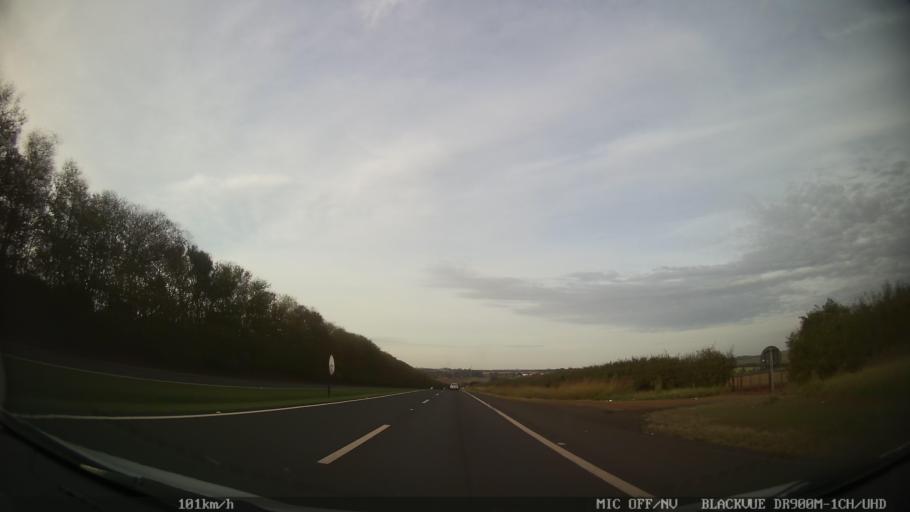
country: BR
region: Sao Paulo
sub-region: Iracemapolis
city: Iracemapolis
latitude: -22.6668
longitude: -47.5366
